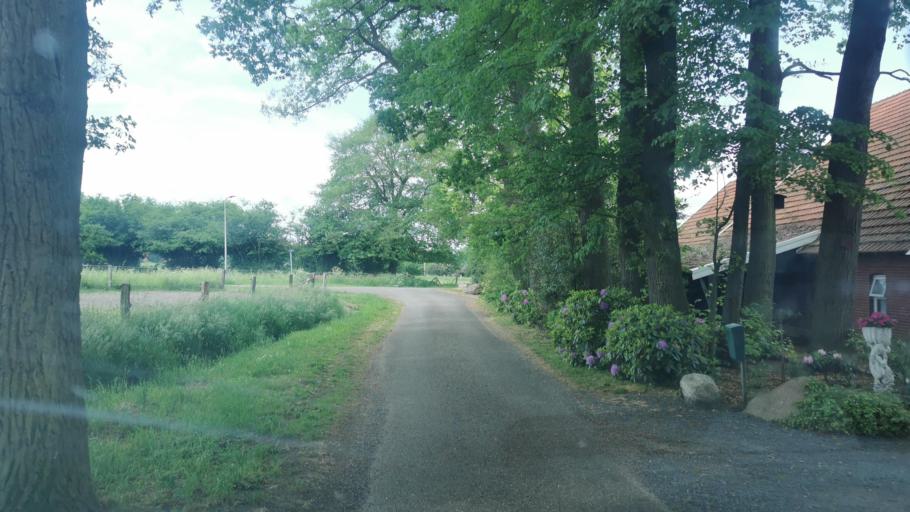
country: NL
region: Overijssel
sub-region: Gemeente Enschede
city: Enschede
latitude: 52.2537
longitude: 6.9053
